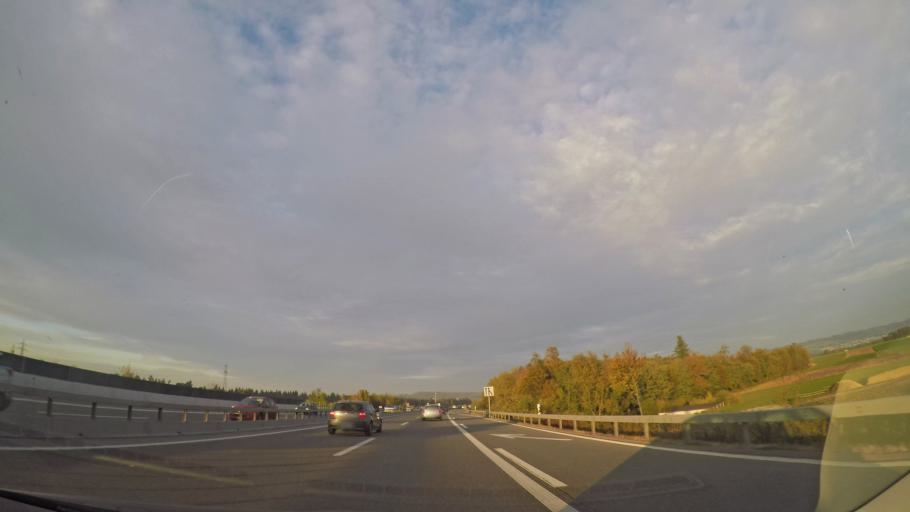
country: CH
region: Aargau
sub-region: Bezirk Lenzburg
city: Othmarsingen
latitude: 47.4183
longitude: 8.2243
